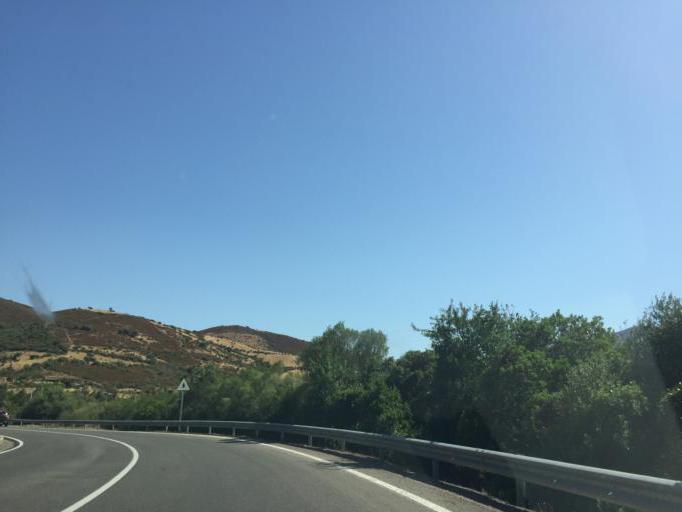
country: IT
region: Sardinia
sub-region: Provincia di Olbia-Tempio
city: San Teodoro
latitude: 40.7317
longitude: 9.6492
